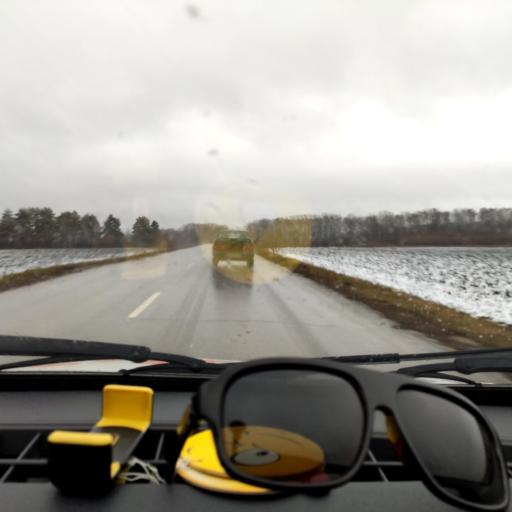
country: RU
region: Bashkortostan
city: Iglino
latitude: 54.8787
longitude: 56.5401
